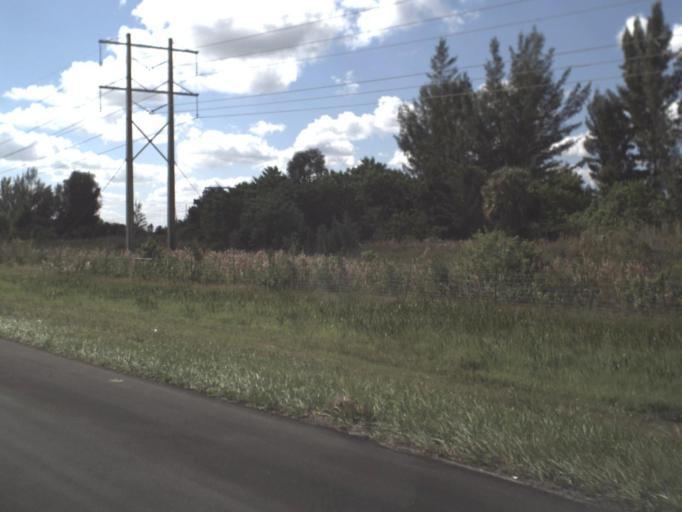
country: US
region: Florida
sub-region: Broward County
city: Tamarac
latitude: 26.1778
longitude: -80.3094
